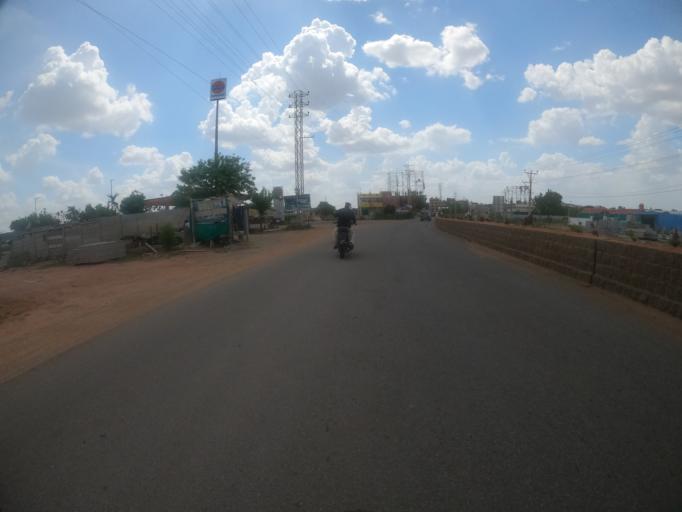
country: IN
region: Telangana
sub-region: Rangareddi
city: Sriramnagar
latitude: 17.3057
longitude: 78.1454
